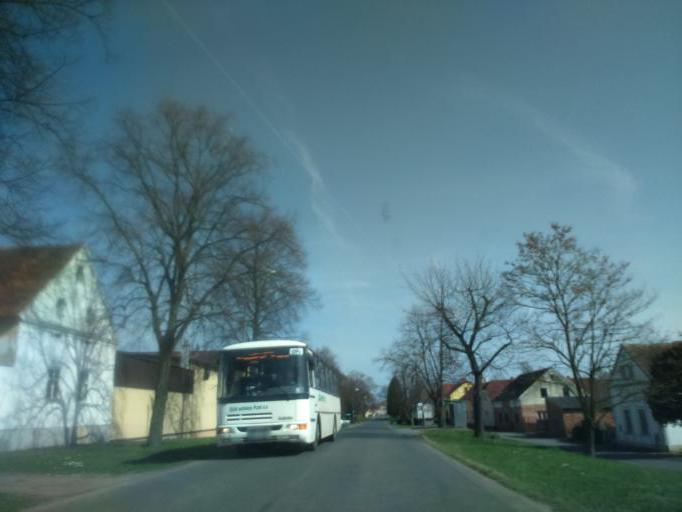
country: CZ
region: Plzensky
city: Hermanova Hut'
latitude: 49.7029
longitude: 13.1264
